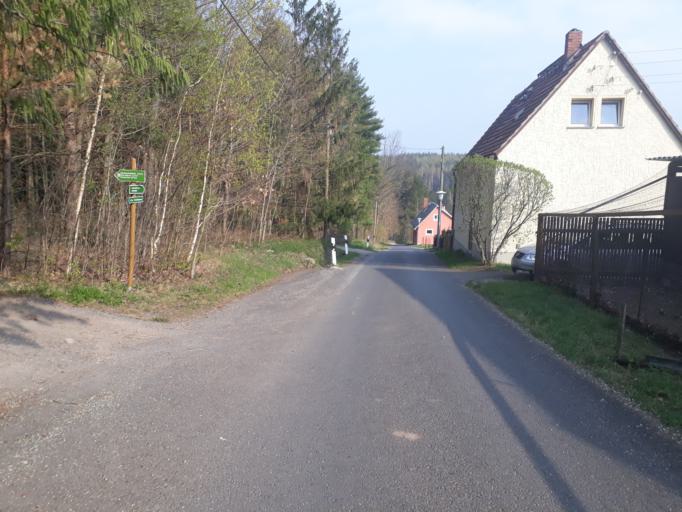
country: DE
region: Saxony
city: Reinhardtsgrimma
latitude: 50.8925
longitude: 13.7744
